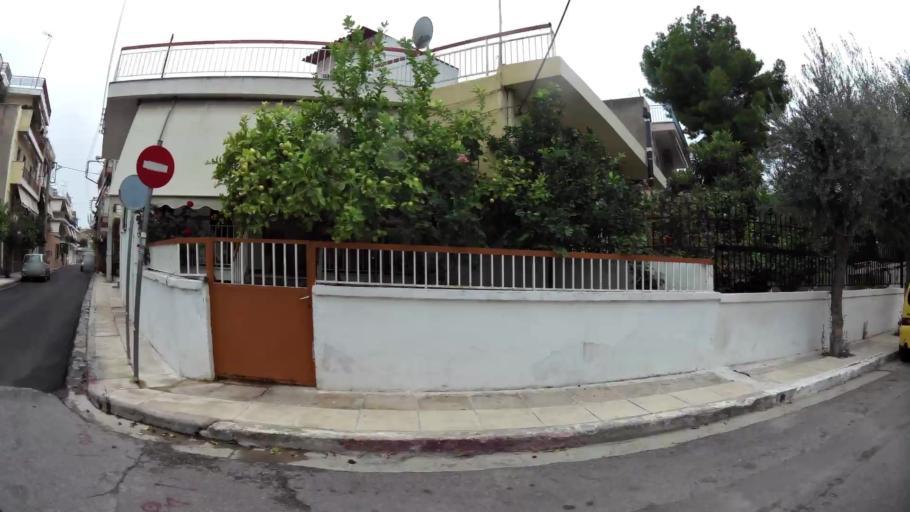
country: GR
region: Attica
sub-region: Nomarchia Athinas
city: Aigaleo
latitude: 37.9835
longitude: 23.6742
